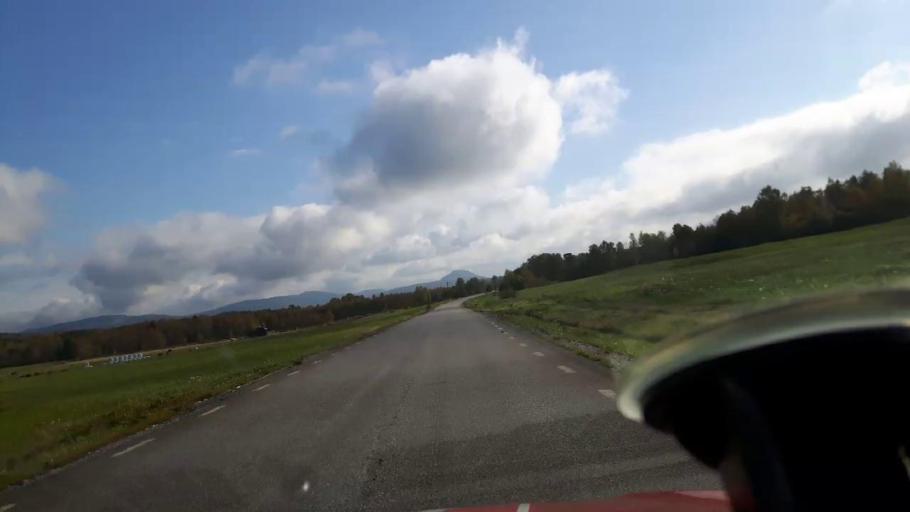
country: SE
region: Gaevleborg
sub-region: Ljusdals Kommun
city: Ljusdal
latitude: 61.7606
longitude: 16.0881
